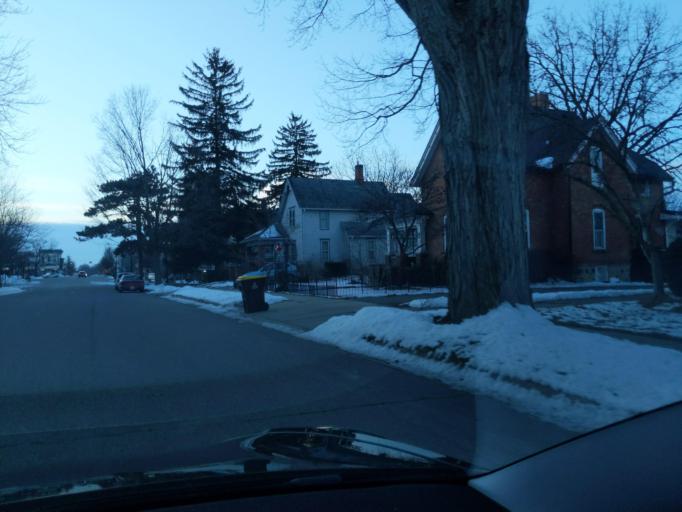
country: US
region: Michigan
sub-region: Ingham County
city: Mason
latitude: 42.5803
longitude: -84.4404
